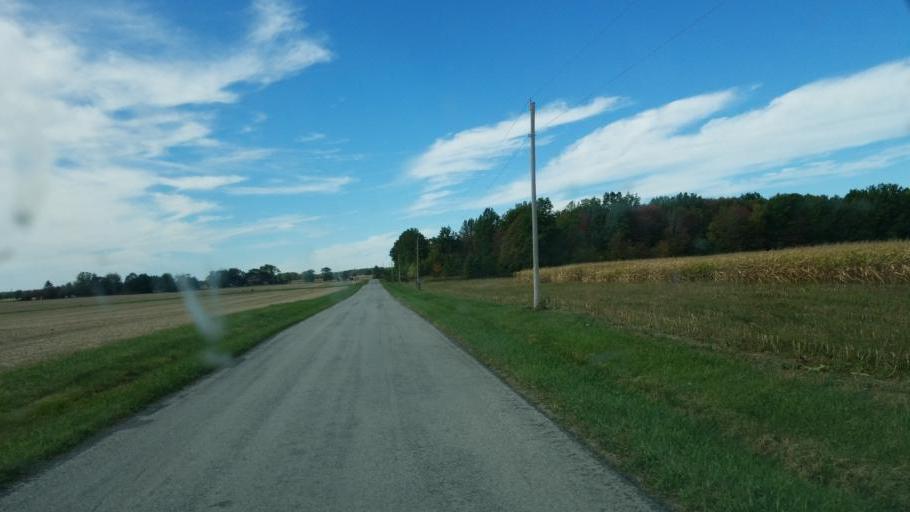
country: US
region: Ohio
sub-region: Huron County
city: Wakeman
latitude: 41.2847
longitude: -82.4847
